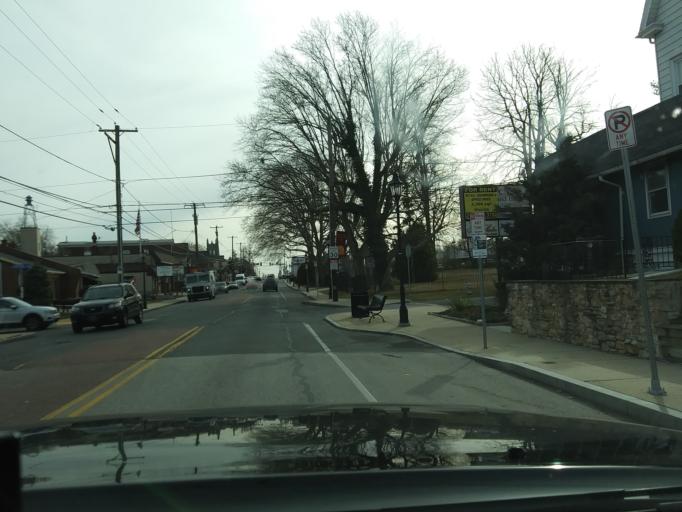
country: US
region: Pennsylvania
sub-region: Montgomery County
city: Rockledge
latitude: 40.0828
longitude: -75.0918
